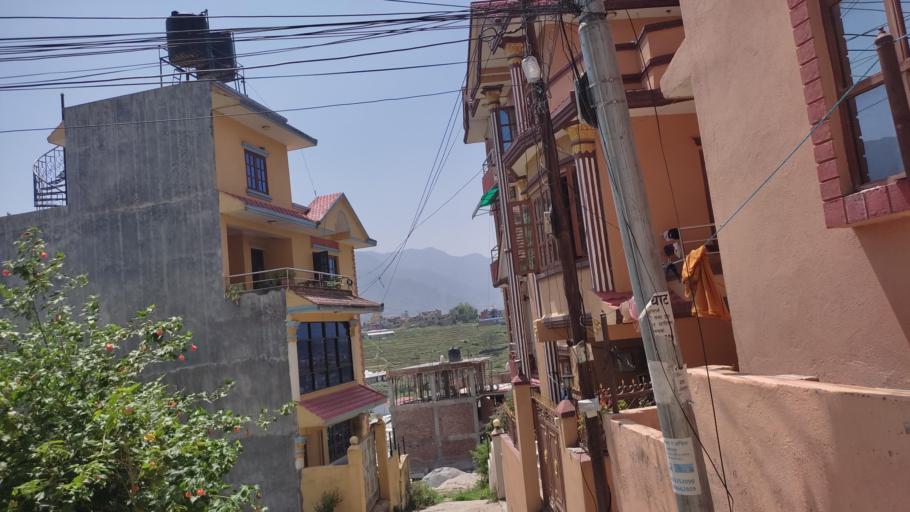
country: NP
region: Central Region
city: Kirtipur
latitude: 27.6754
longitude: 85.2715
